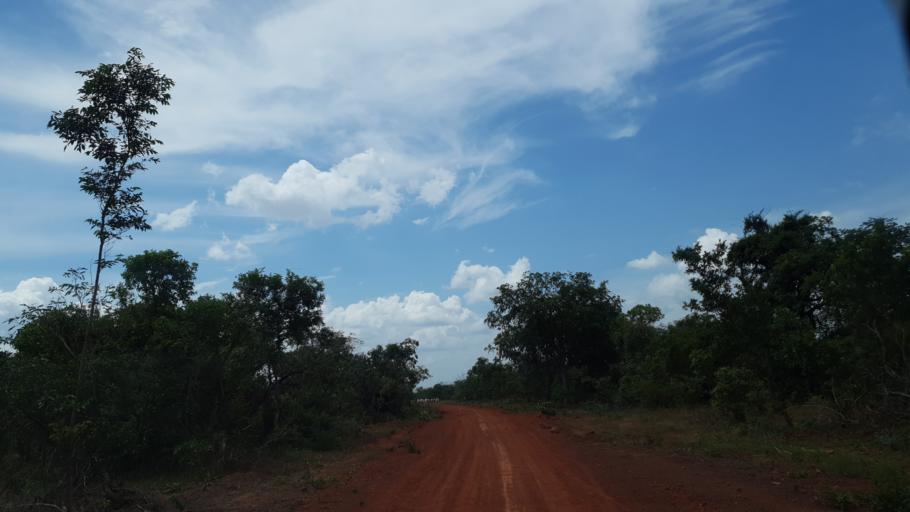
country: ML
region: Sikasso
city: Sikasso
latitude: 11.6863
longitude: -6.2109
